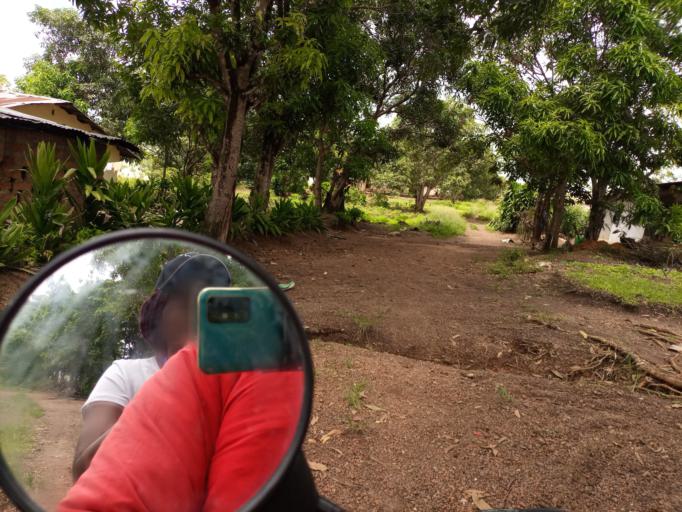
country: SL
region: Southern Province
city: Baoma
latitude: 7.9727
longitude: -11.7145
